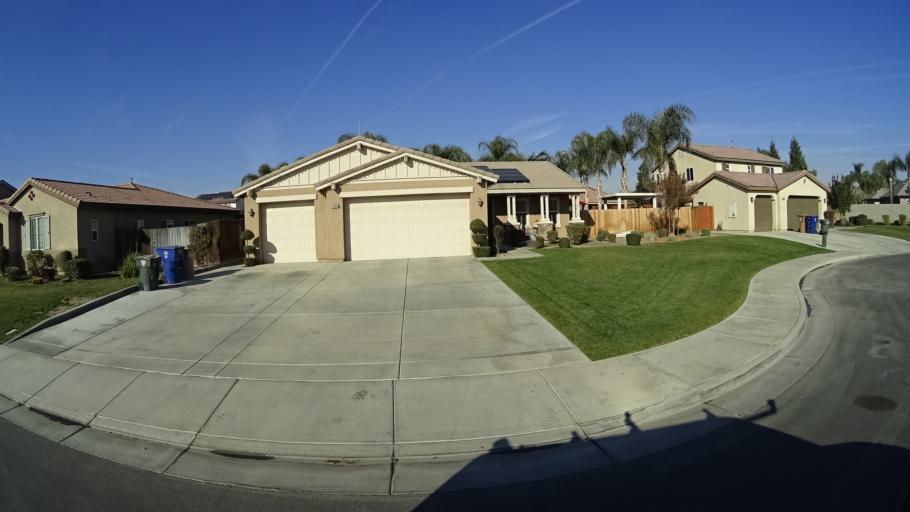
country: US
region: California
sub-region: Kern County
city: Greenfield
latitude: 35.2837
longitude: -119.0528
